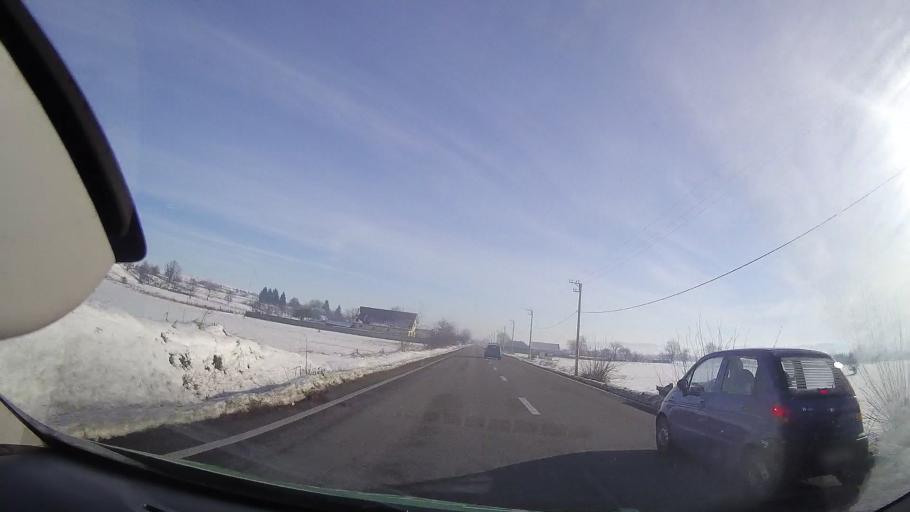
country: RO
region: Neamt
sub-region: Comuna Ghindaoani
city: Ghindaoani
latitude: 47.0813
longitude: 26.3433
